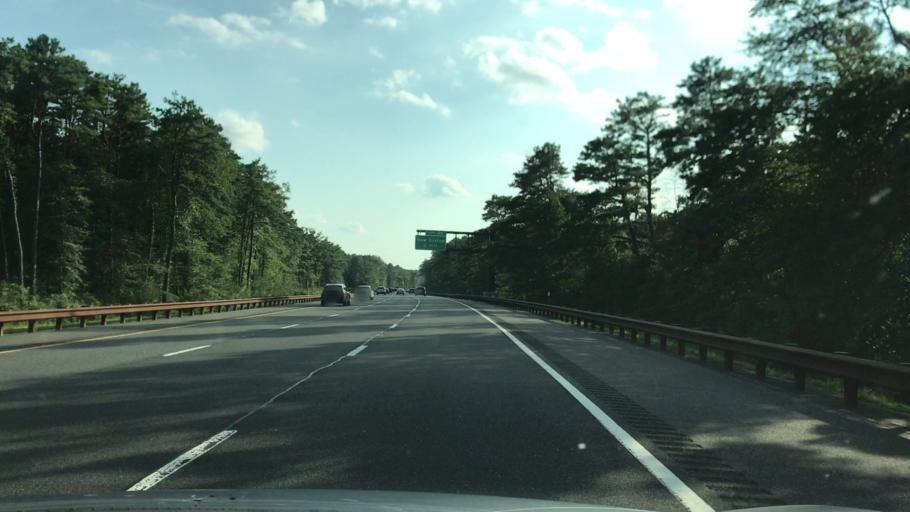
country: US
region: New Jersey
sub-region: Ocean County
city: Tuckerton
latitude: 39.6246
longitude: -74.3992
